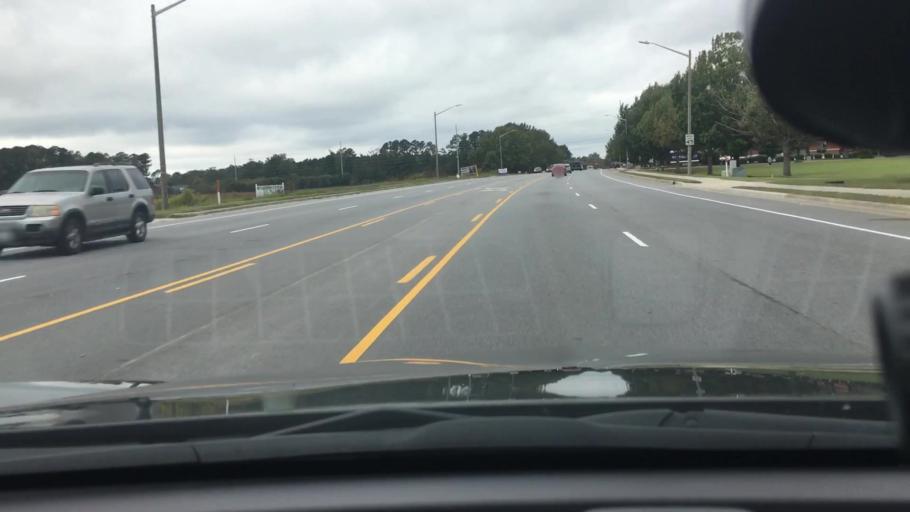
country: US
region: North Carolina
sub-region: Pitt County
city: Summerfield
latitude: 35.5969
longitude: -77.4054
